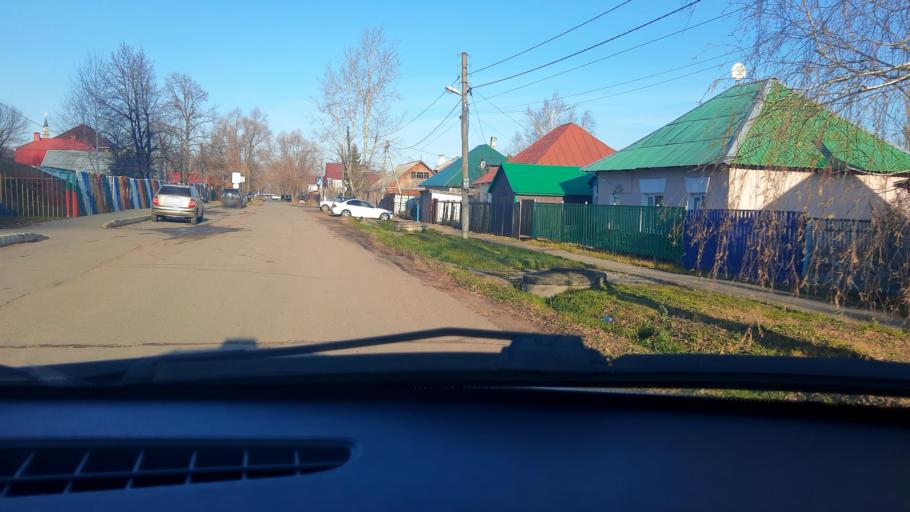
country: RU
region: Bashkortostan
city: Avdon
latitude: 54.6977
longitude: 55.8237
